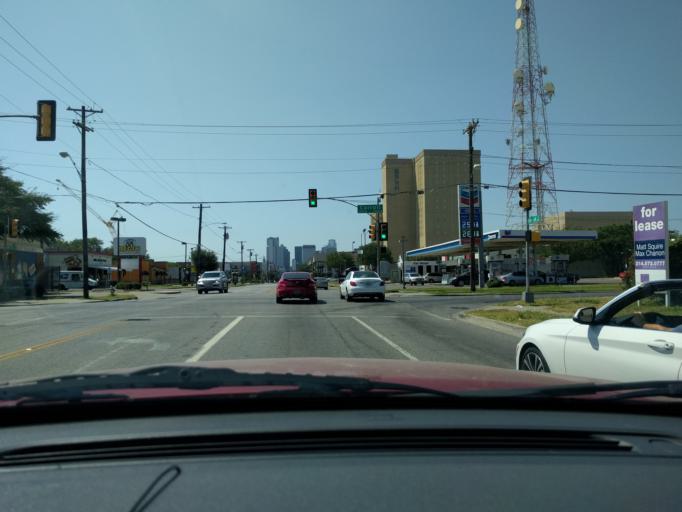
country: US
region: Texas
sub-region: Dallas County
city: Dallas
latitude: 32.7995
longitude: -96.7763
